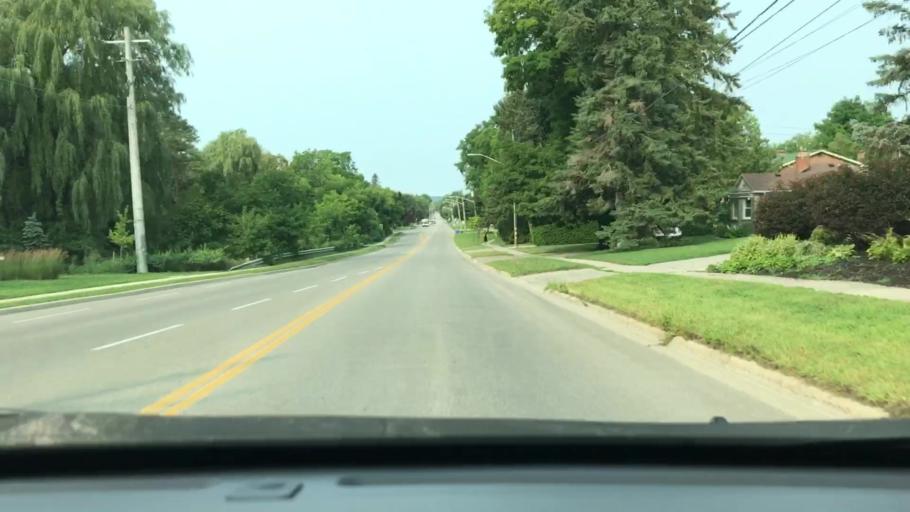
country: CA
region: Ontario
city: Newmarket
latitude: 44.0554
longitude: -79.4362
